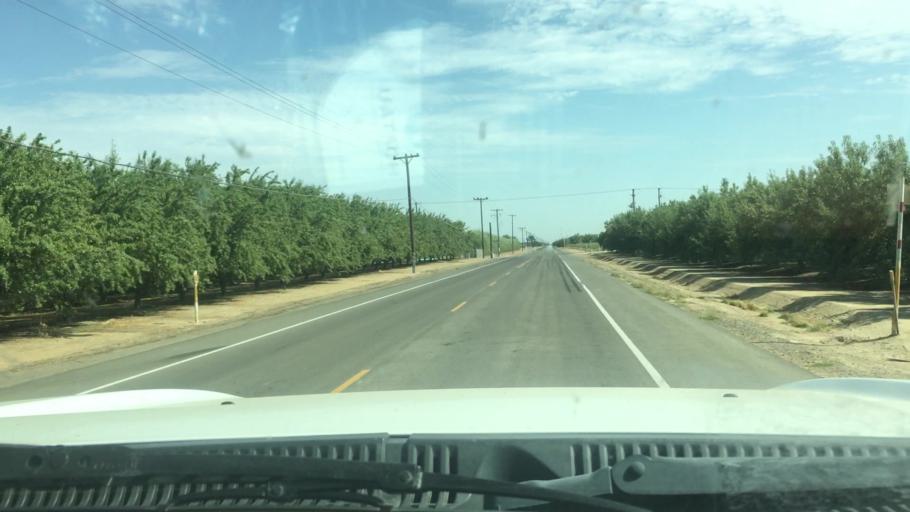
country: US
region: California
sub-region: Kern County
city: Wasco
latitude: 35.5563
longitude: -119.4742
